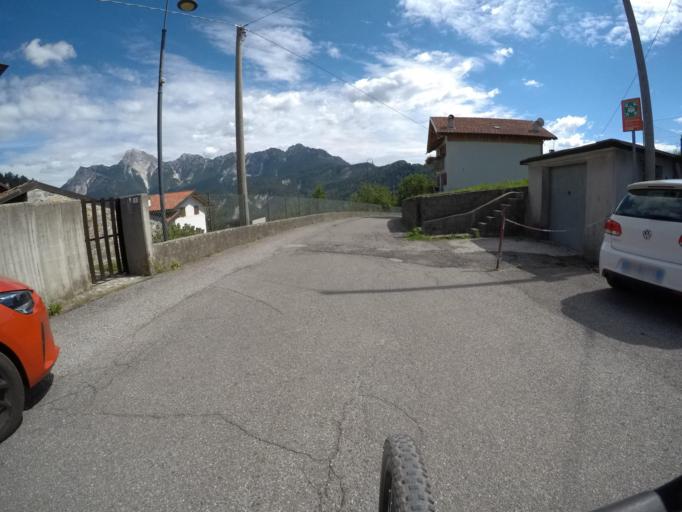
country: IT
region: Friuli Venezia Giulia
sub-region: Provincia di Udine
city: Zuglio
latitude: 46.4654
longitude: 13.0367
